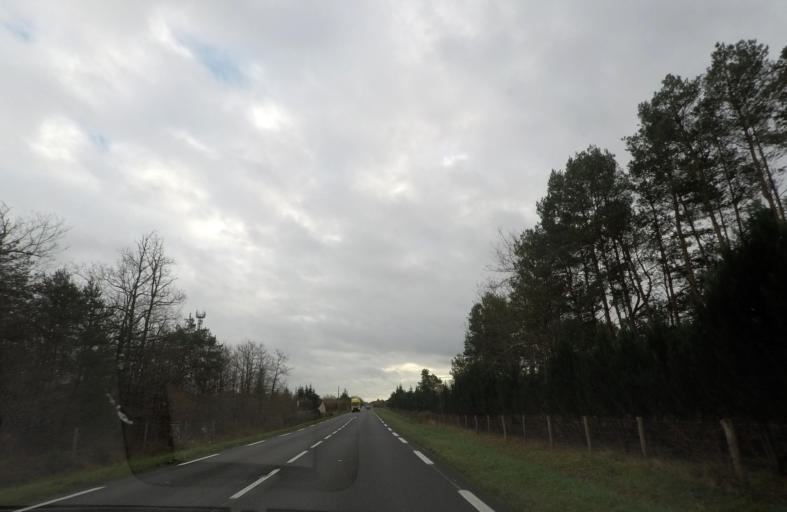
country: FR
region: Centre
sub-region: Departement du Loir-et-Cher
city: Soings-en-Sologne
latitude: 47.4673
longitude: 1.5116
